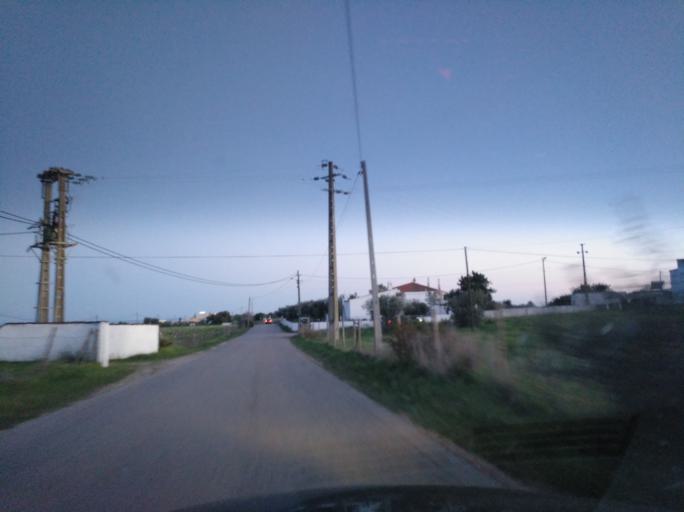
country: PT
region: Faro
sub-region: Vila Real de Santo Antonio
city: Monte Gordo
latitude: 37.1877
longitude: -7.5097
